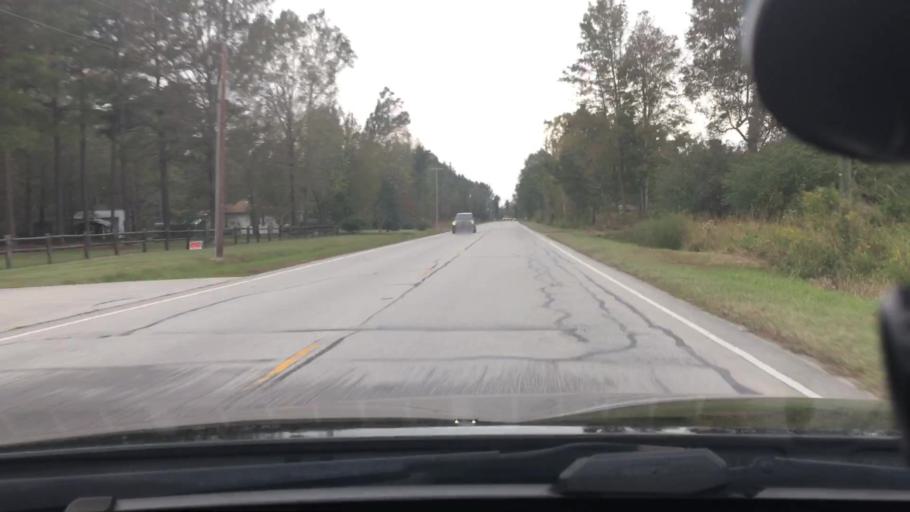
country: US
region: North Carolina
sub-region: Craven County
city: Vanceboro
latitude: 35.3223
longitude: -77.1661
